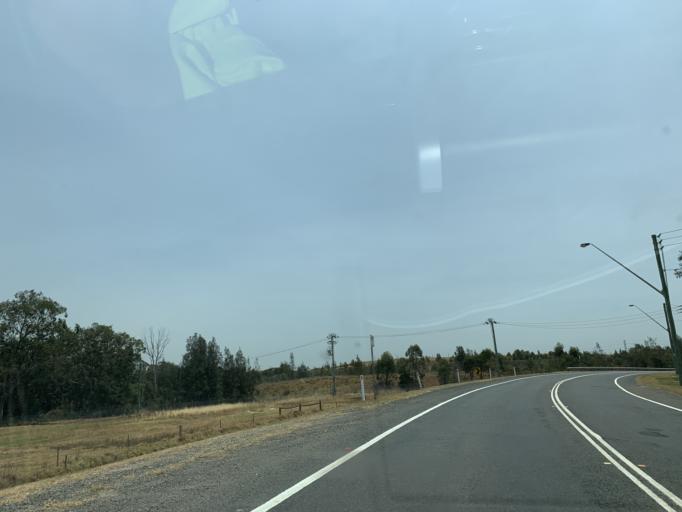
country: AU
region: New South Wales
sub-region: Fairfield
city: Horsley Park
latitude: -33.8213
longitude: 150.8671
